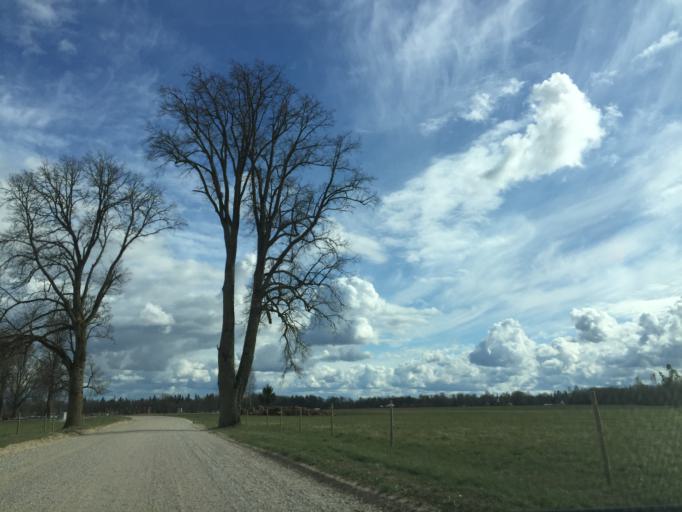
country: LV
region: Burtnieki
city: Matisi
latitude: 57.6064
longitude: 25.0791
